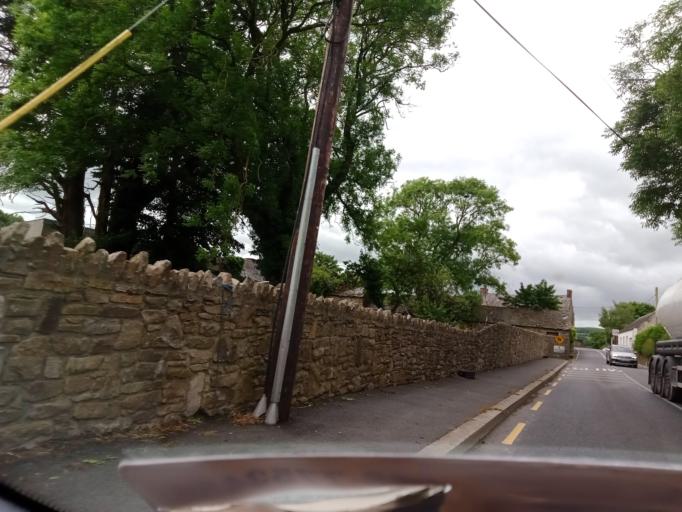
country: IE
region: Leinster
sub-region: Kilkenny
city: Thomastown
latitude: 52.4717
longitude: -7.2626
